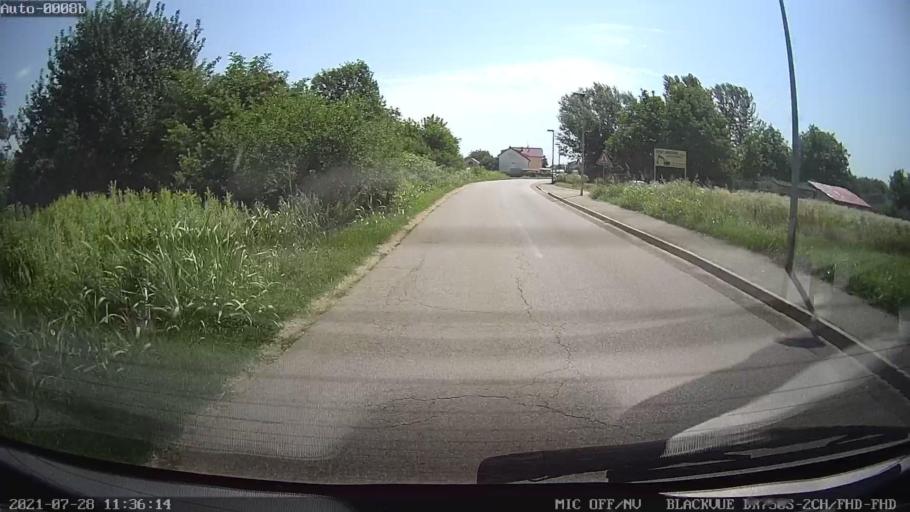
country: HR
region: Varazdinska
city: Varazdin
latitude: 46.2996
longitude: 16.3616
